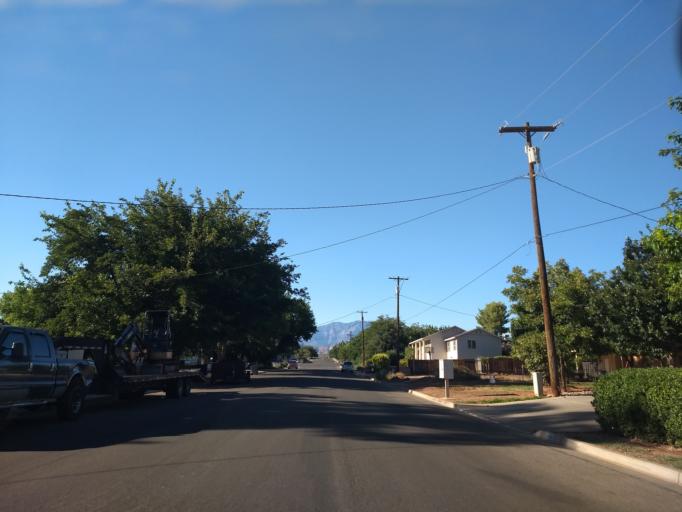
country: US
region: Utah
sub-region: Washington County
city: Washington
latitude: 37.1342
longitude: -113.5065
